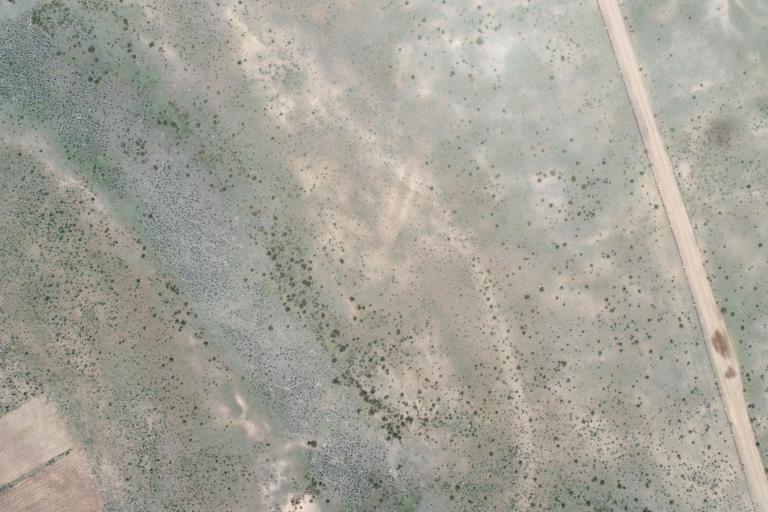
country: BO
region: La Paz
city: Curahuara de Carangas
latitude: -17.2800
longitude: -68.5154
